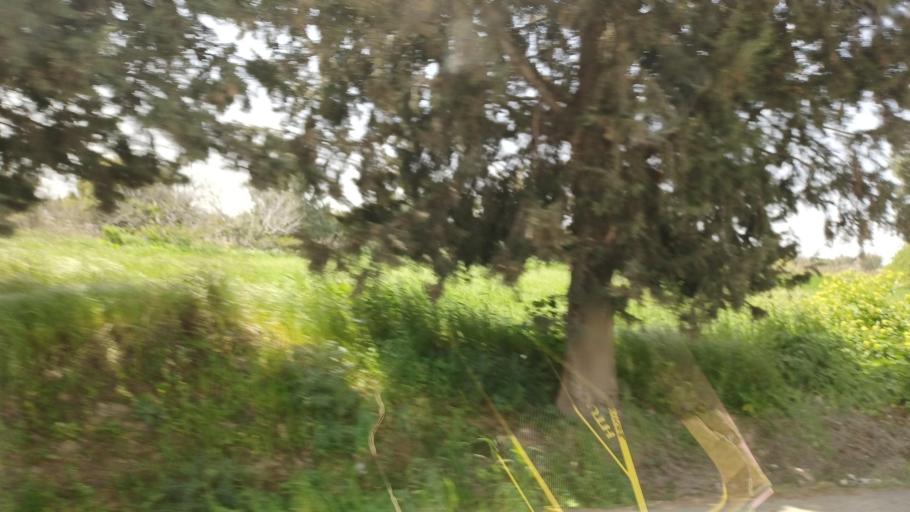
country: CY
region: Limassol
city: Pissouri
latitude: 34.7338
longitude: 32.7357
